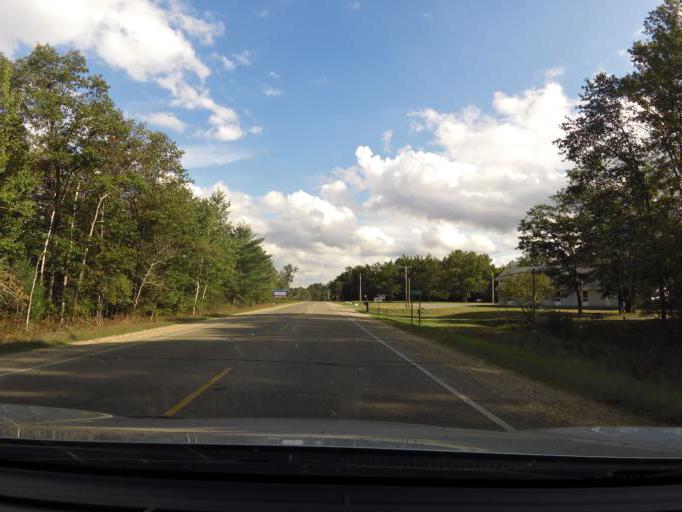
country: US
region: Michigan
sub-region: Roscommon County
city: Saint Helen
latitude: 44.3767
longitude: -84.4160
